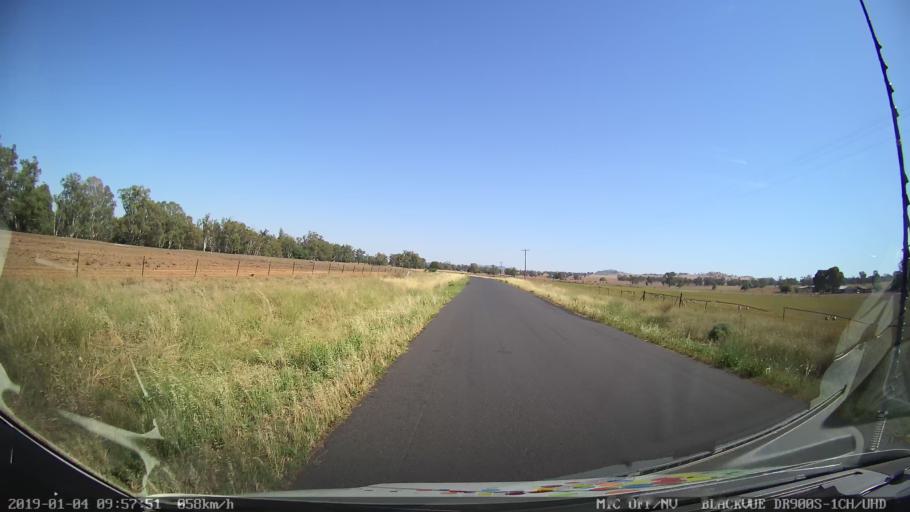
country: AU
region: New South Wales
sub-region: Cabonne
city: Canowindra
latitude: -33.5240
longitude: 148.3983
